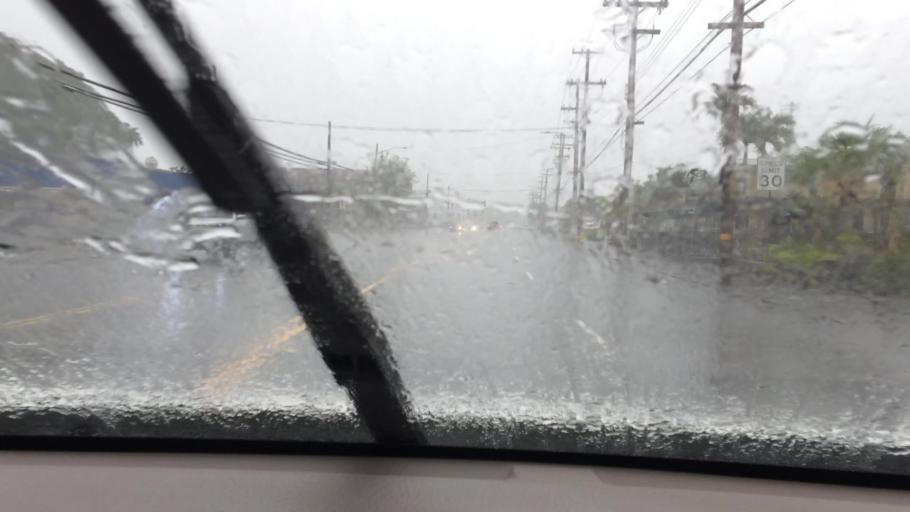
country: US
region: Hawaii
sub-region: Hawaii County
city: Hilo
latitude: 19.7199
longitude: -155.0827
